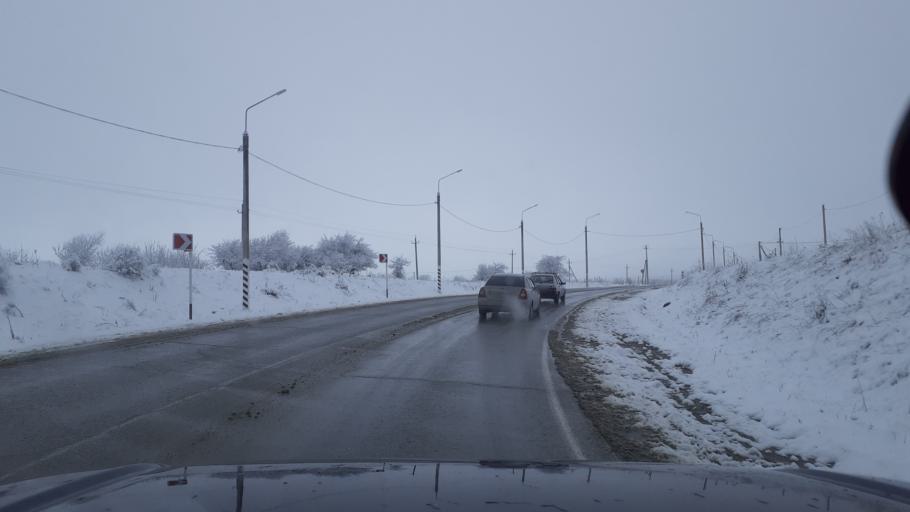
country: RU
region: Adygeya
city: Tul'skiy
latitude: 44.4972
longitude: 40.1728
